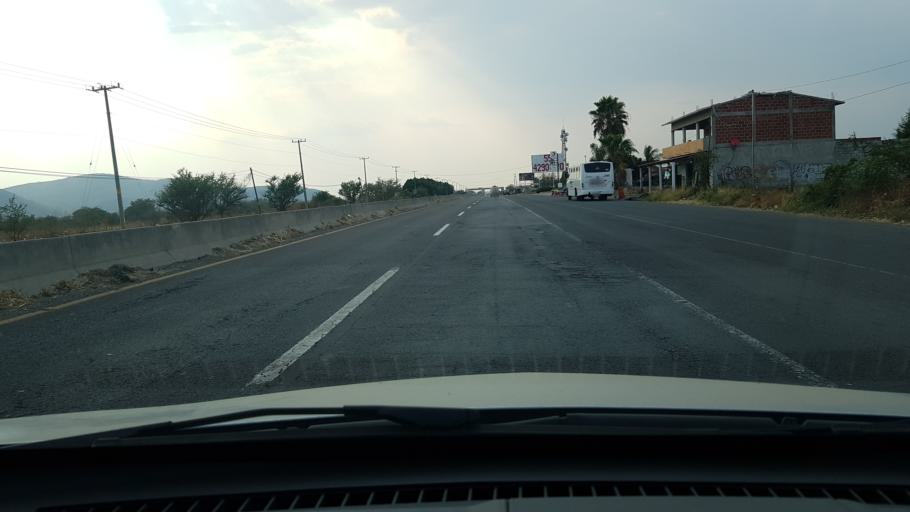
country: MX
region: Morelos
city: Amayuca
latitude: 18.7355
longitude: -98.8208
